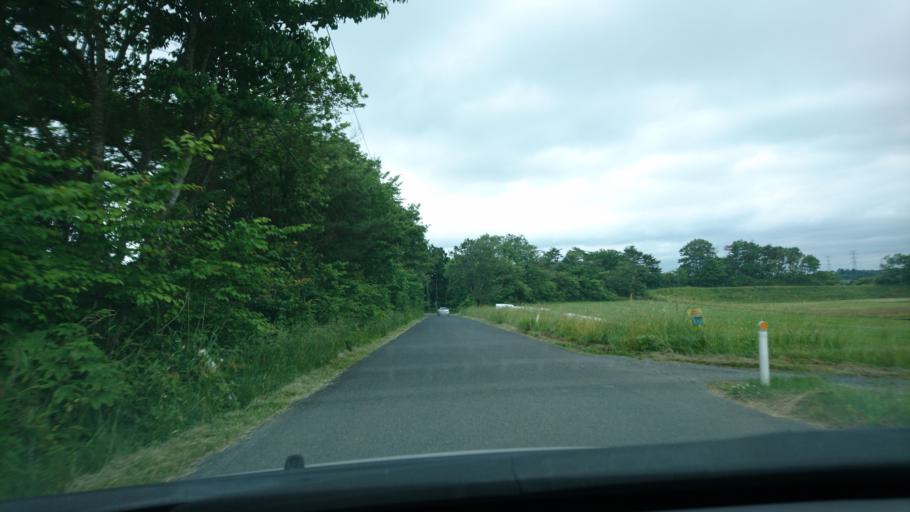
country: JP
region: Iwate
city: Ichinoseki
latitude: 38.8784
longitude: 141.2011
